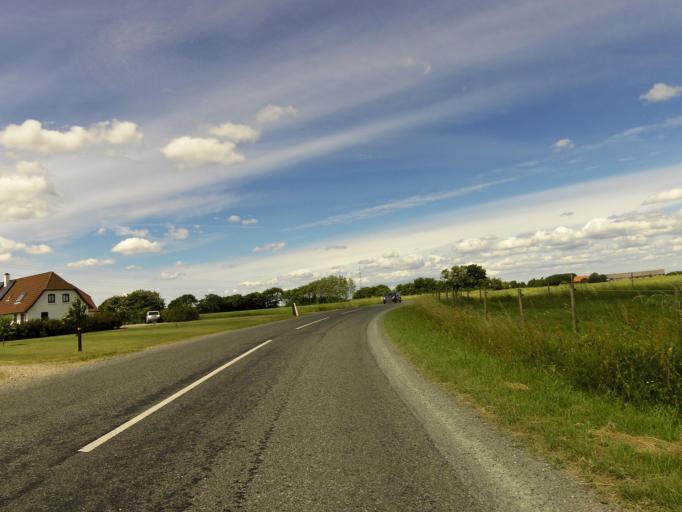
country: DK
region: South Denmark
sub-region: Esbjerg Kommune
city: Ribe
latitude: 55.2664
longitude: 8.8083
